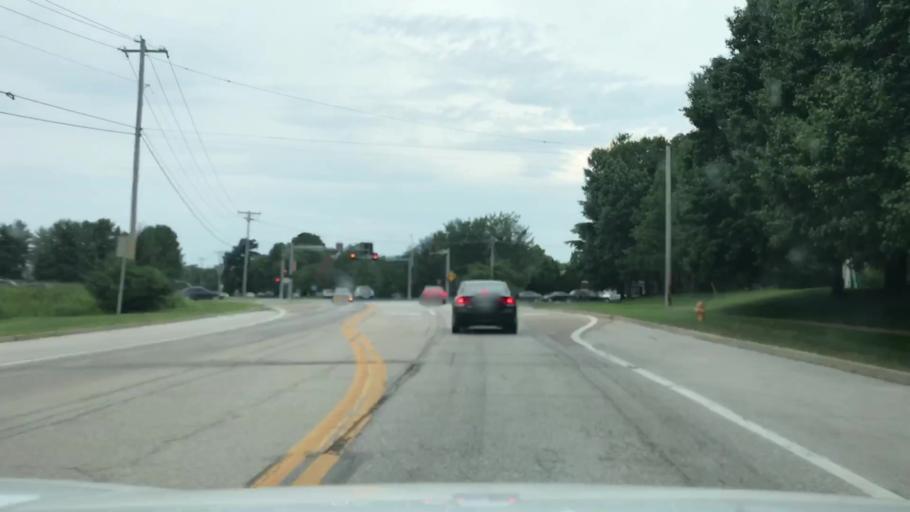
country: US
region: Missouri
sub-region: Saint Louis County
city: Chesterfield
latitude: 38.6602
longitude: -90.5803
